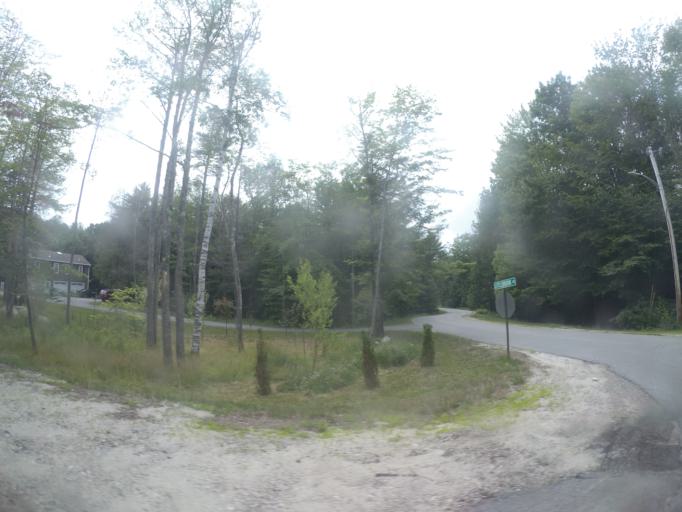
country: US
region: Maine
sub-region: Cumberland County
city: Falmouth
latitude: 43.7604
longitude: -70.2429
